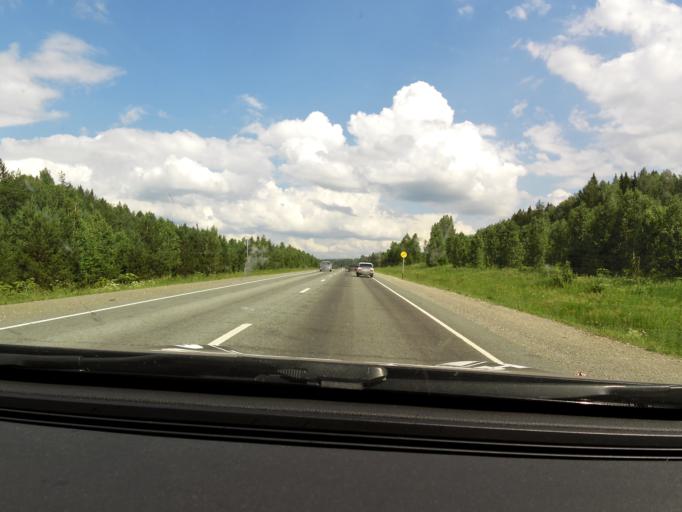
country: RU
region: Sverdlovsk
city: Arti
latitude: 56.7968
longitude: 58.6384
